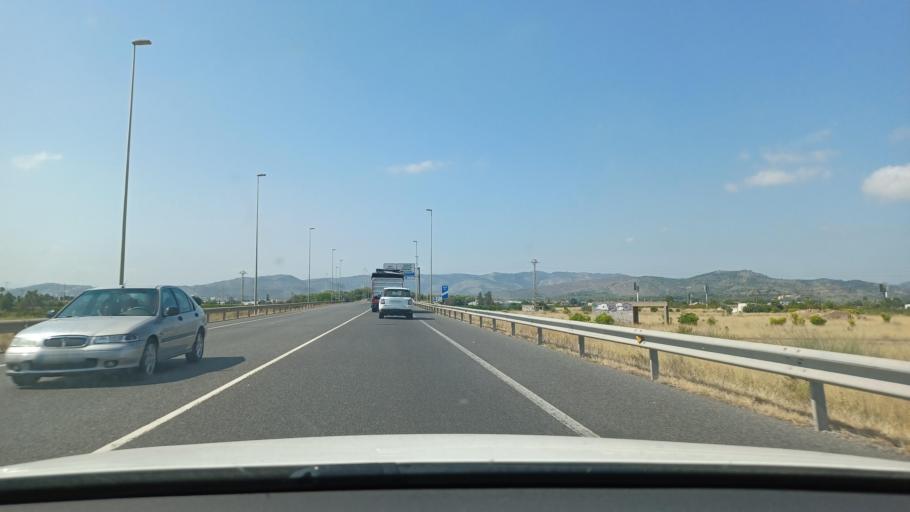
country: ES
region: Valencia
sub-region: Provincia de Castello
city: Almassora
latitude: 39.9788
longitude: -0.0871
